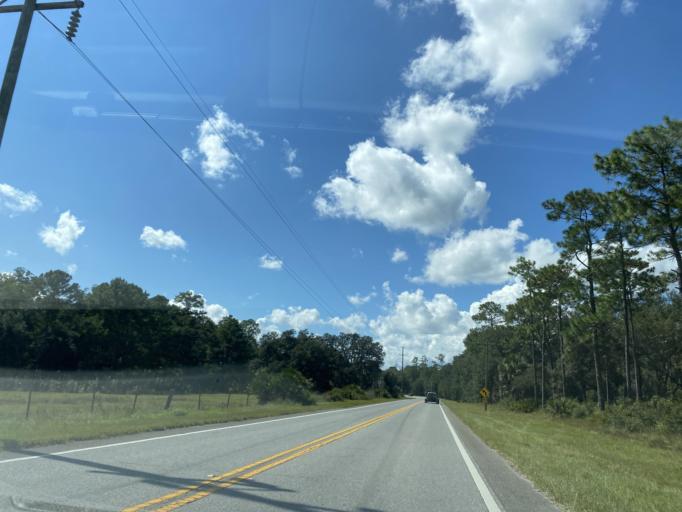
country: US
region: Florida
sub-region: Lake County
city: Umatilla
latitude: 28.9748
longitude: -81.5506
